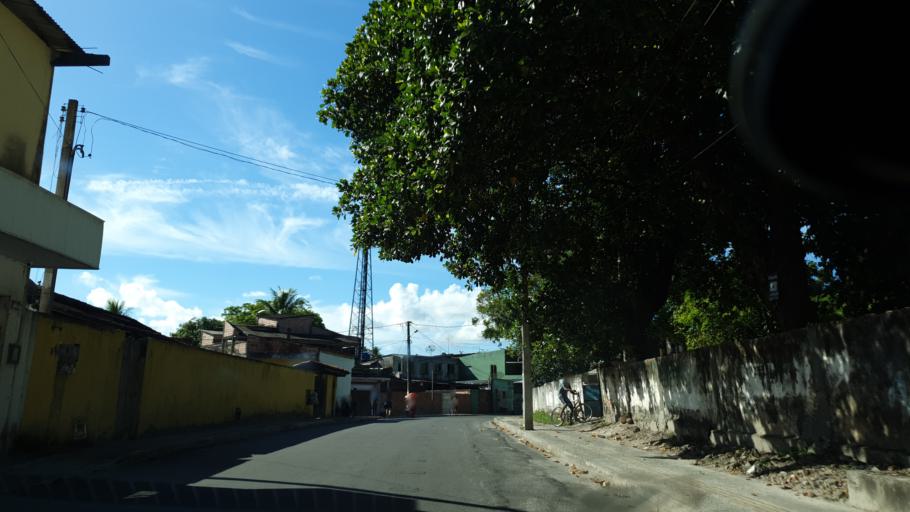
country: BR
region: Bahia
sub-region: Mata De Sao Joao
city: Mata de Sao Joao
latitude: -12.6155
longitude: -38.2959
